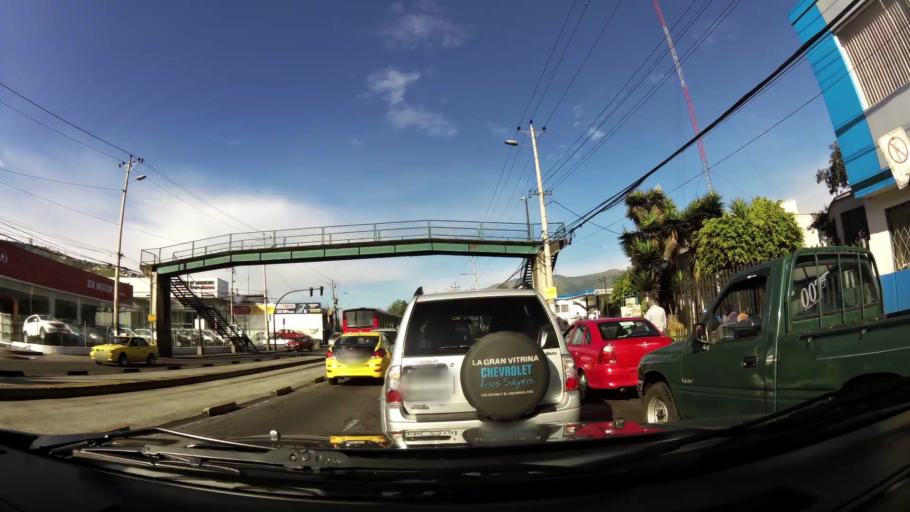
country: EC
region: Pichincha
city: Quito
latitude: -0.2702
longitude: -78.5283
